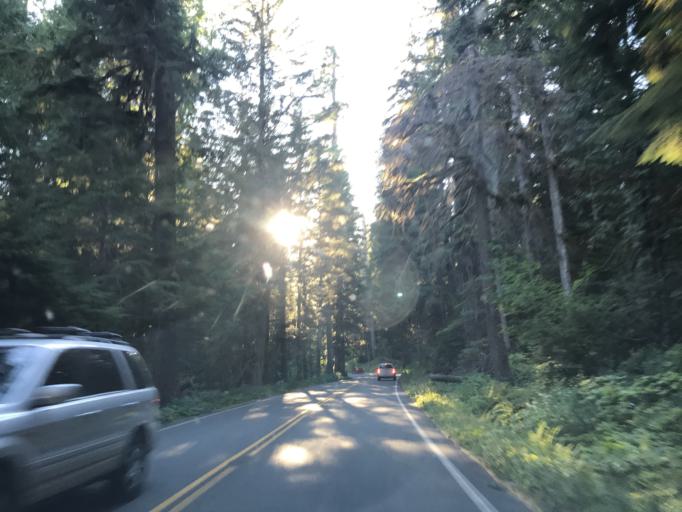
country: US
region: Washington
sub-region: Pierce County
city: Eatonville
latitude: 46.7347
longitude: -121.8448
